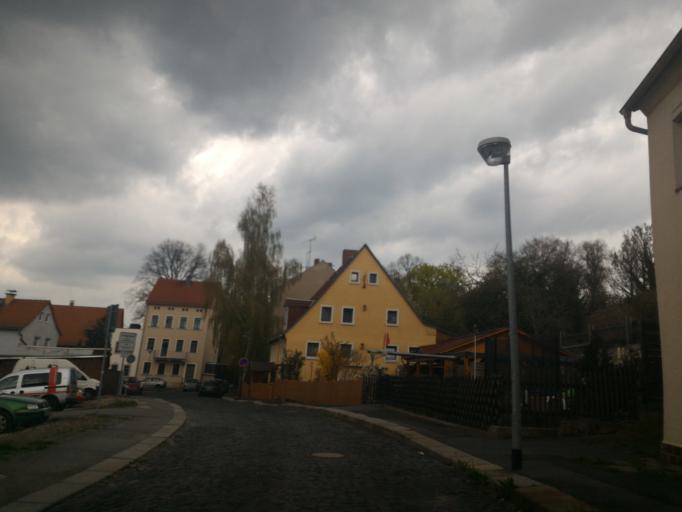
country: DE
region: Saxony
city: Zittau
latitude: 50.8995
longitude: 14.8042
